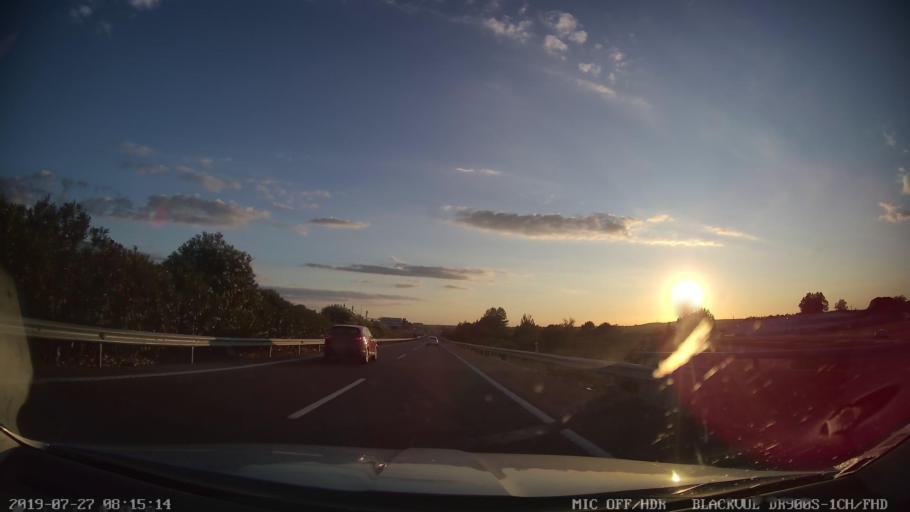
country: ES
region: Extremadura
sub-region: Provincia de Badajoz
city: Calamonte
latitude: 38.9070
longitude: -6.3917
